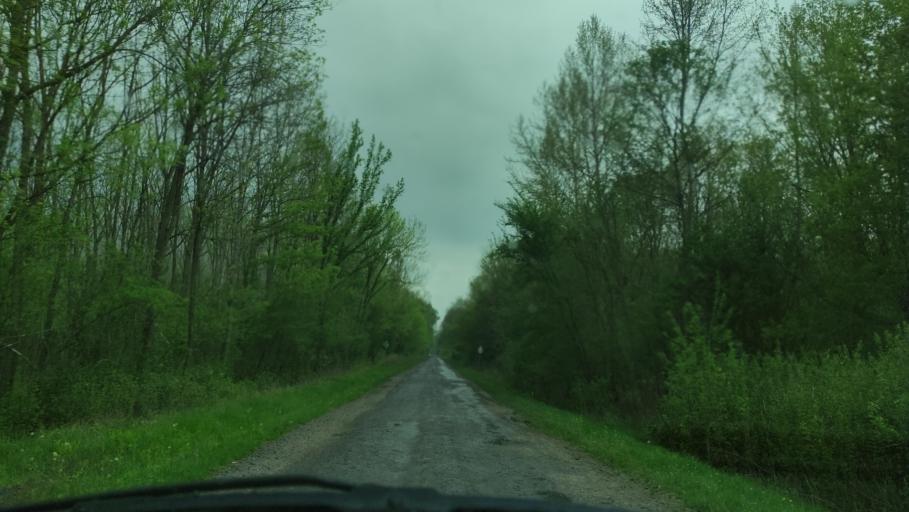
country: HU
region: Baranya
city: Mohacs
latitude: 45.9181
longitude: 18.7292
